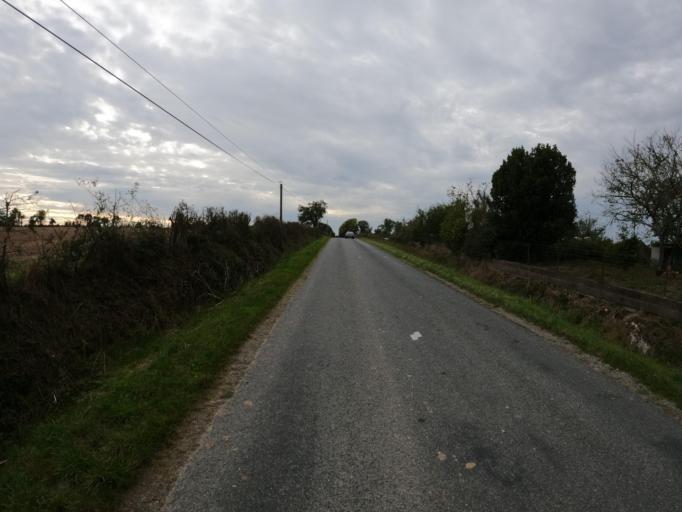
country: FR
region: Pays de la Loire
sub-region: Departement de Maine-et-Loire
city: Saint-Christophe-du-Bois
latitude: 47.0227
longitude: -0.9787
